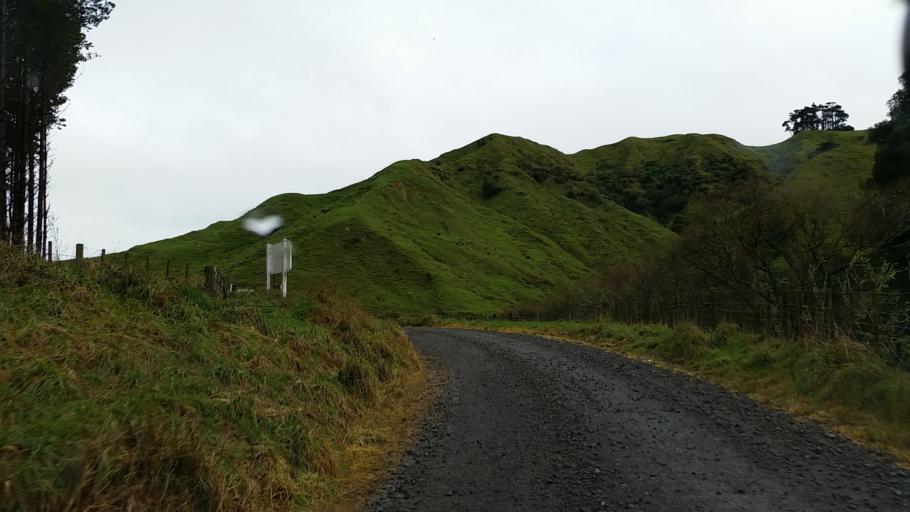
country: NZ
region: Taranaki
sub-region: South Taranaki District
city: Eltham
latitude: -39.5020
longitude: 174.4061
